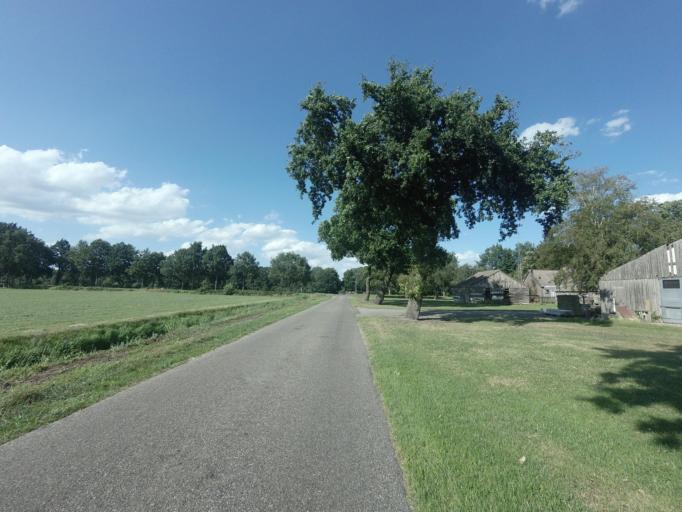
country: NL
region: Drenthe
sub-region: Gemeente Hoogeveen
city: Hoogeveen
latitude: 52.6701
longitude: 6.5158
